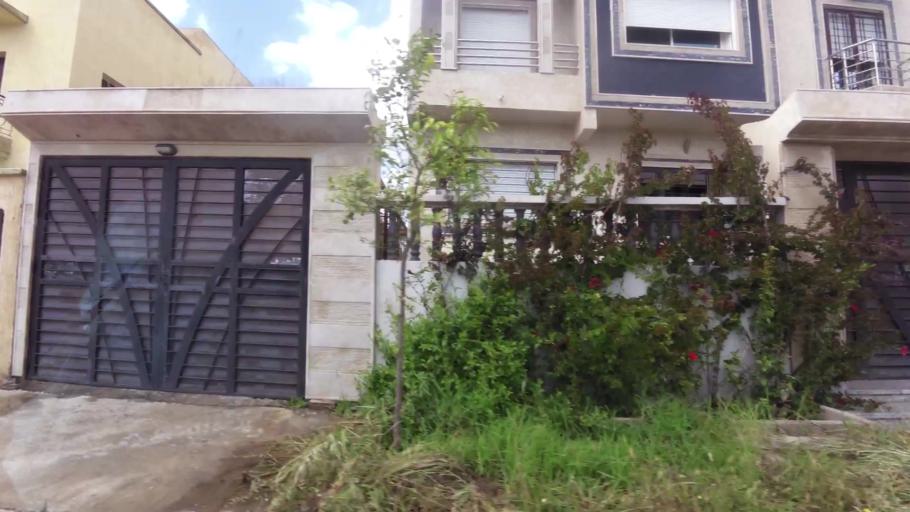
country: MA
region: Chaouia-Ouardigha
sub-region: Settat Province
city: Berrechid
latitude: 33.2787
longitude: -7.5922
